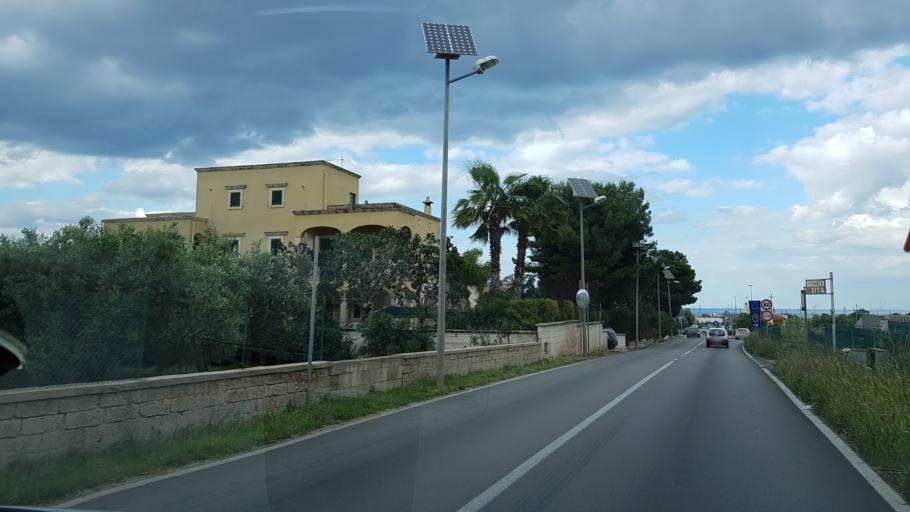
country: IT
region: Apulia
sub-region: Provincia di Brindisi
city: Fasano
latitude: 40.8483
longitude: 17.3851
